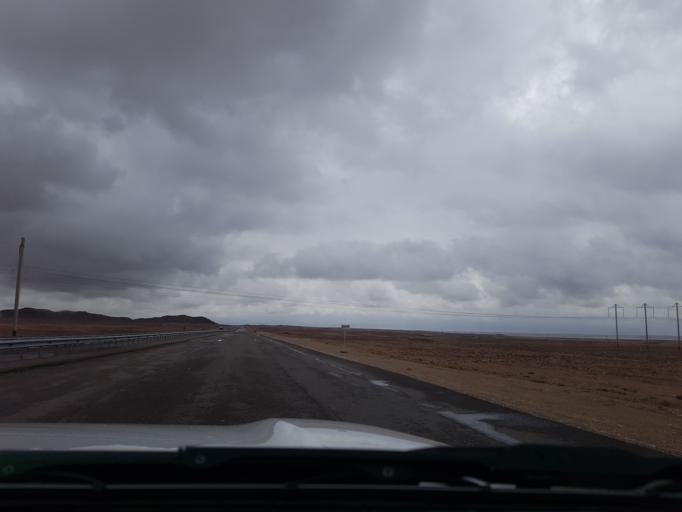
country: TM
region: Balkan
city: Balkanabat
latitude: 39.9285
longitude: 53.8666
